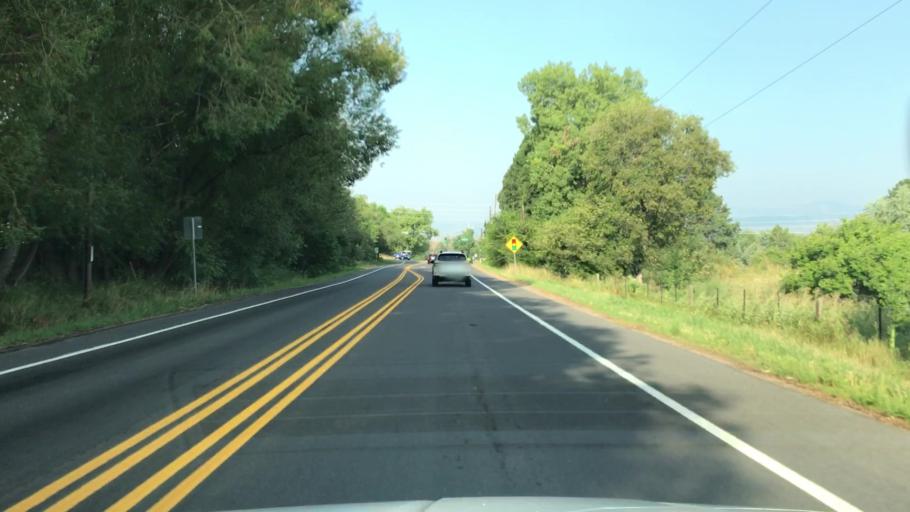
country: US
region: Colorado
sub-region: Boulder County
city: Gunbarrel
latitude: 40.0337
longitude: -105.1763
